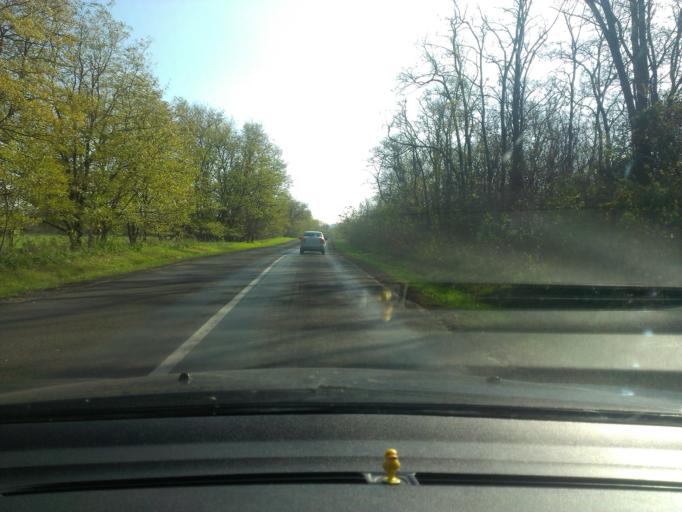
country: HU
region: Komarom-Esztergom
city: Naszaly
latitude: 47.6835
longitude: 18.2366
